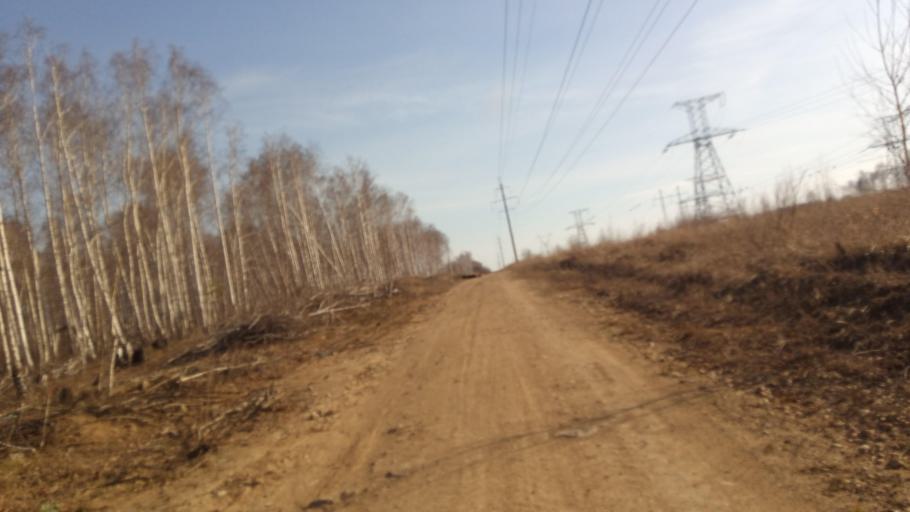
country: RU
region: Chelyabinsk
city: Sargazy
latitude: 55.1180
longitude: 61.2365
